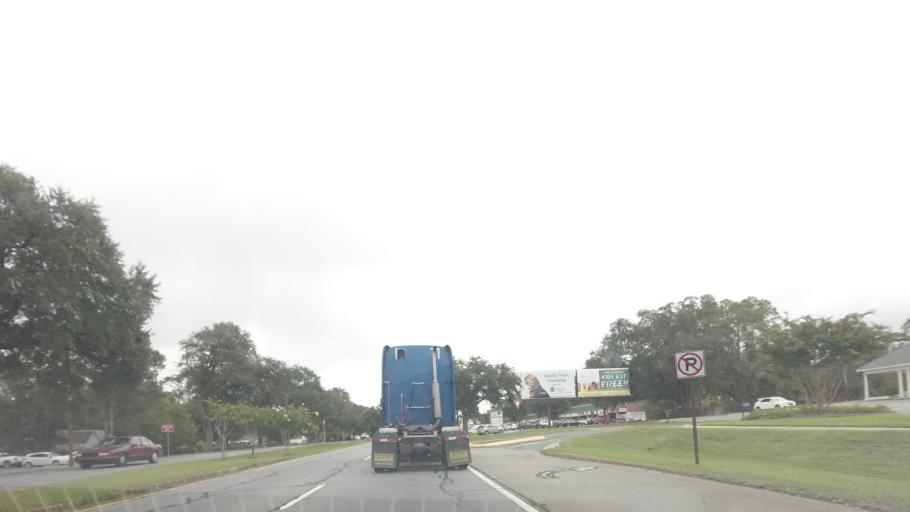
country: US
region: Georgia
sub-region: Laurens County
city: Dublin
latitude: 32.5368
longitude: -82.9338
